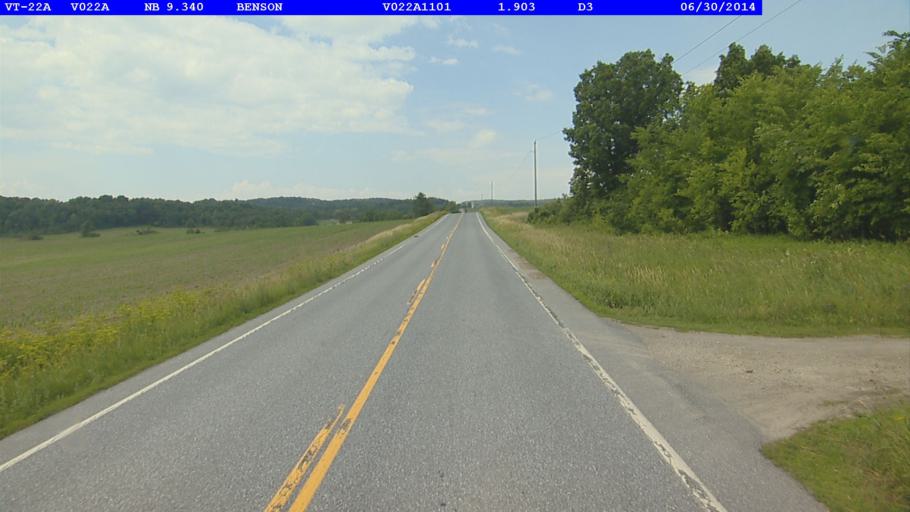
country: US
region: Vermont
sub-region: Rutland County
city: Fair Haven
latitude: 43.6960
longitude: -73.2939
